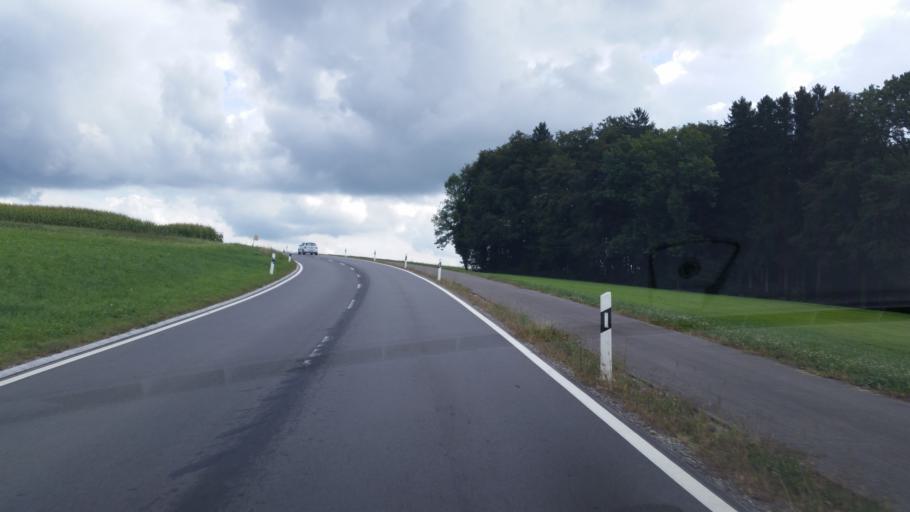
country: CH
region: Zurich
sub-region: Bezirk Affoltern
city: Mettmenstetten
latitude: 47.2426
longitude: 8.4776
